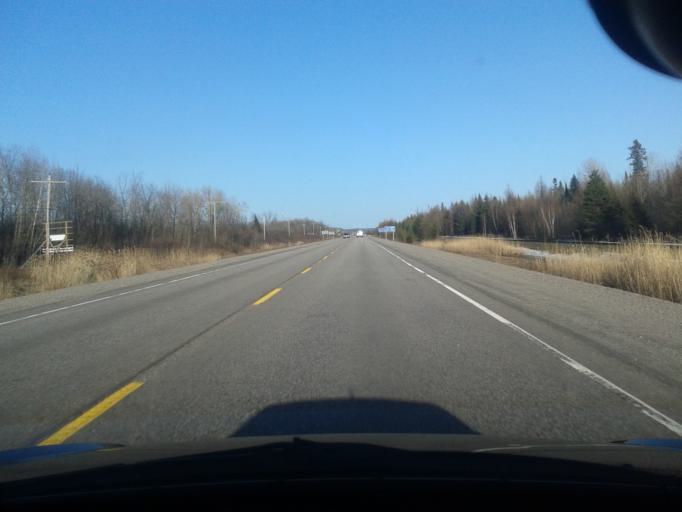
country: CA
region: Ontario
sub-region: Nipissing District
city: North Bay
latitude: 46.3681
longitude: -79.7892
